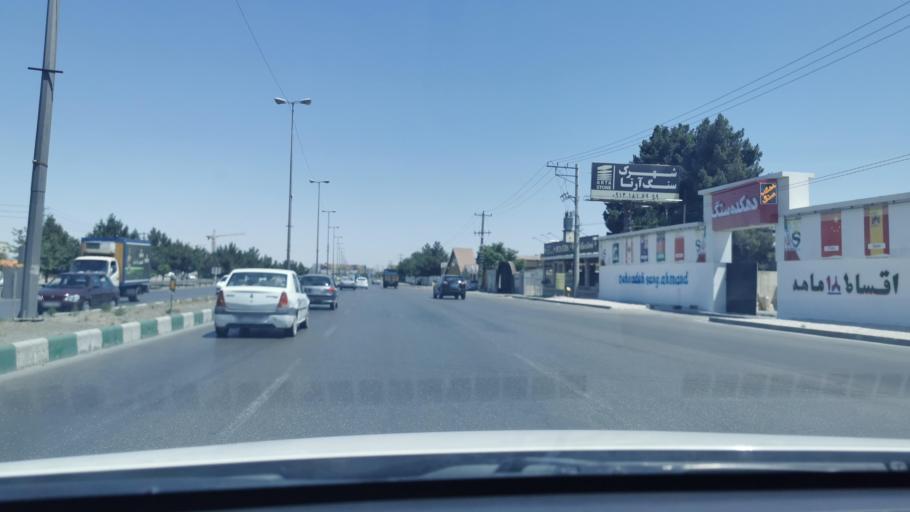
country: IR
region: Razavi Khorasan
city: Mashhad
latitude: 36.4004
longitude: 59.4840
